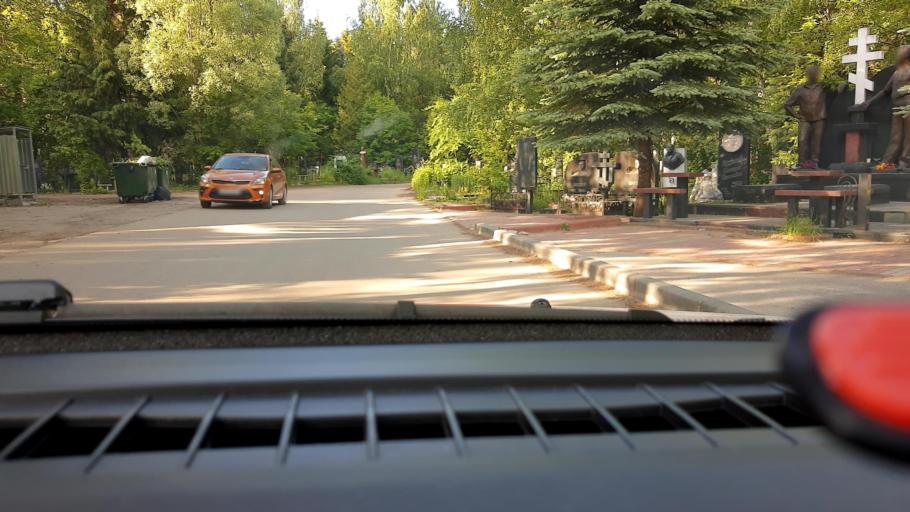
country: RU
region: Nizjnij Novgorod
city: Gorbatovka
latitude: 56.2319
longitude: 43.7624
